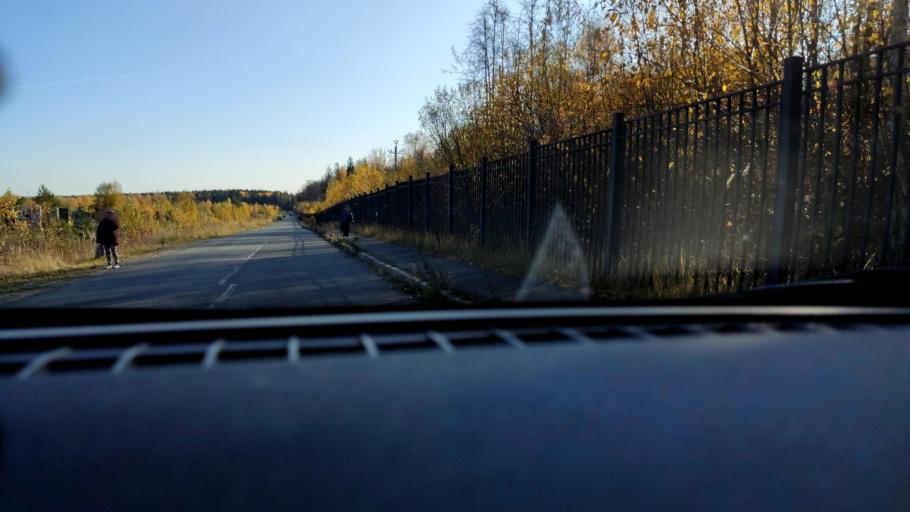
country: RU
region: Perm
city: Kondratovo
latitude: 58.0627
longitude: 56.1454
